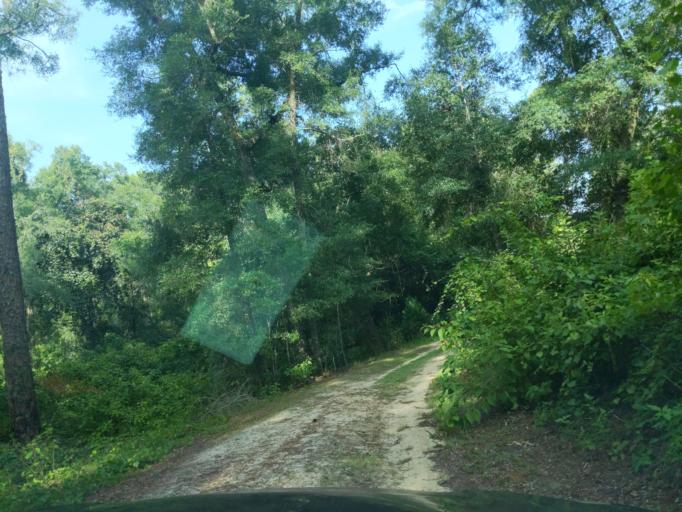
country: US
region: Florida
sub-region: Gadsden County
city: Midway
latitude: 30.4057
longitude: -84.4074
